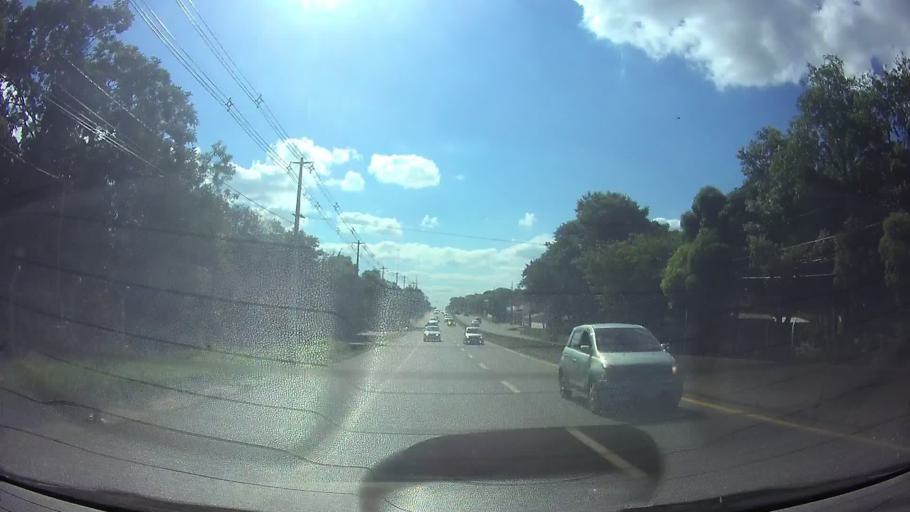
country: PY
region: Central
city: Itaugua
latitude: -25.3997
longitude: -57.3248
